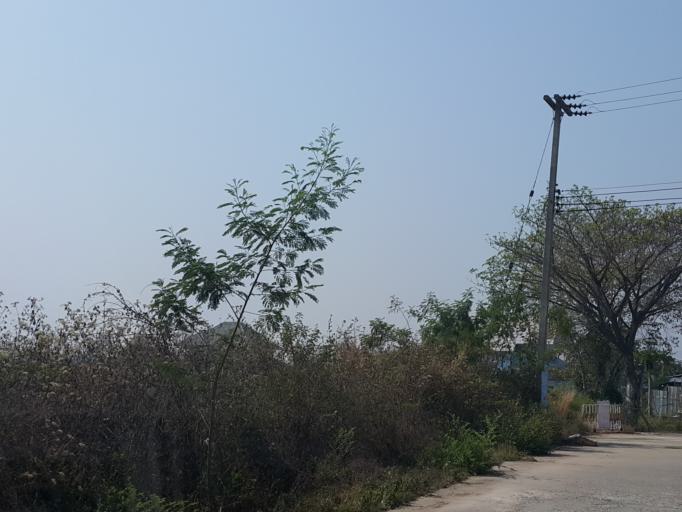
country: TH
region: Chiang Mai
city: San Kamphaeng
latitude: 18.7795
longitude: 99.0744
